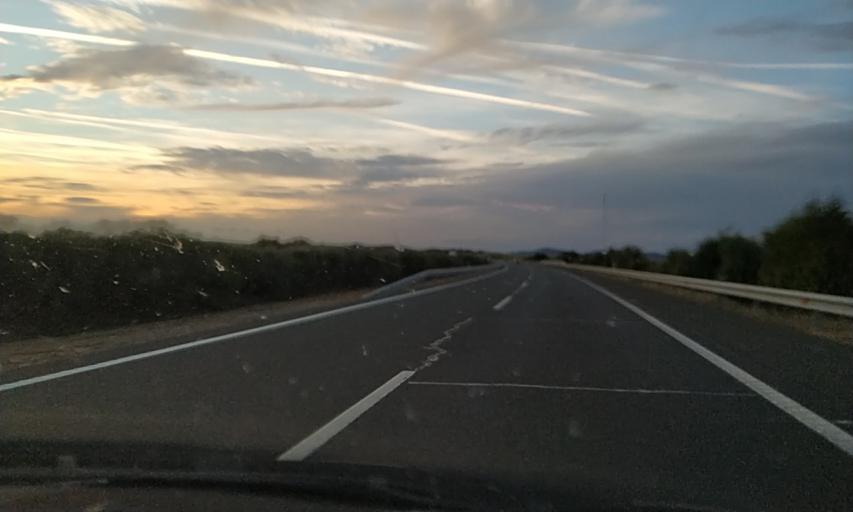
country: ES
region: Extremadura
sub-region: Provincia de Caceres
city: Aldea del Cano
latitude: 39.3328
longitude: -6.3326
